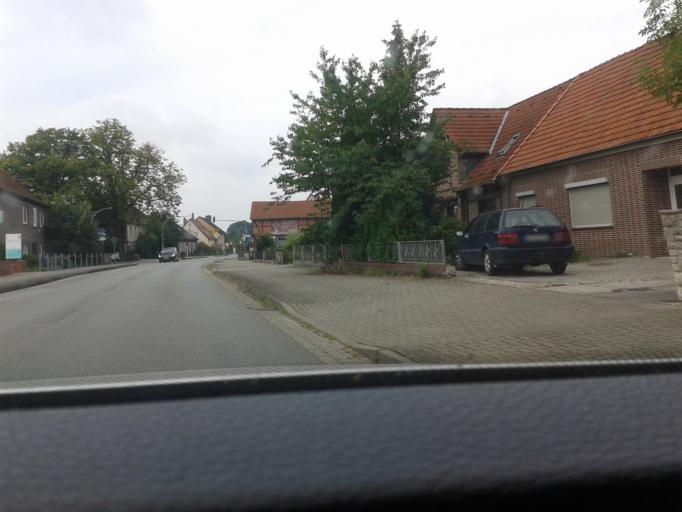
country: DE
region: Lower Saxony
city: Osloss
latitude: 52.4691
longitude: 10.6813
